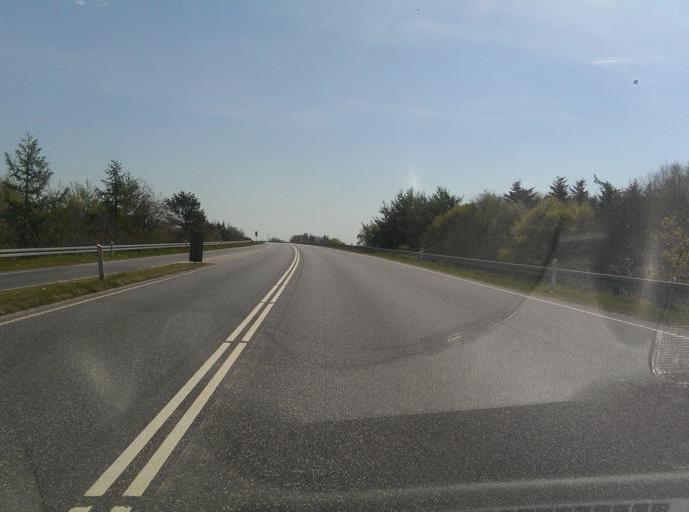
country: DK
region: South Denmark
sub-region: Esbjerg Kommune
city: Ribe
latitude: 55.3901
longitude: 8.7405
